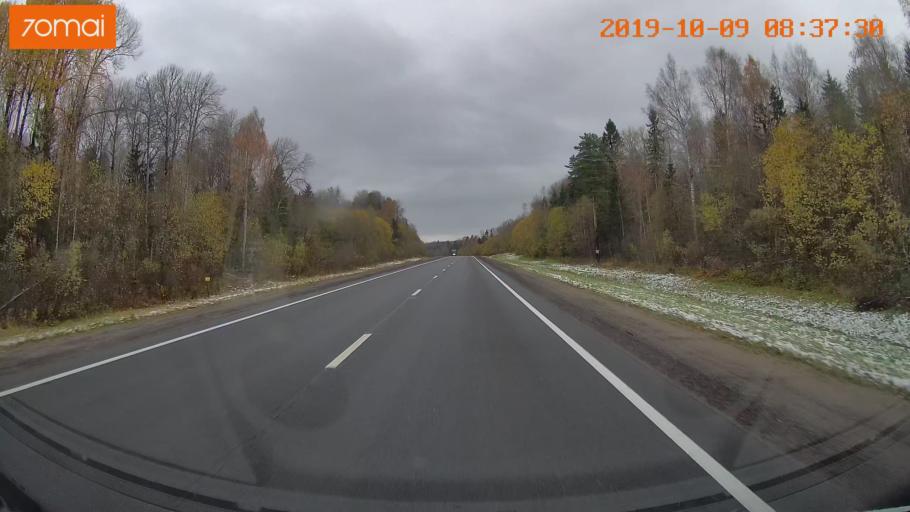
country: RU
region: Vologda
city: Gryazovets
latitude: 58.9423
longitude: 40.1742
